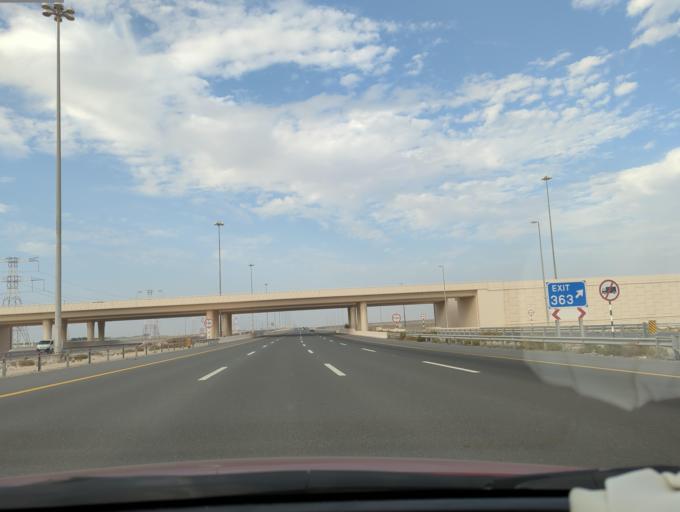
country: AE
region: Abu Dhabi
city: Abu Dhabi
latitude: 24.4596
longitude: 54.7499
